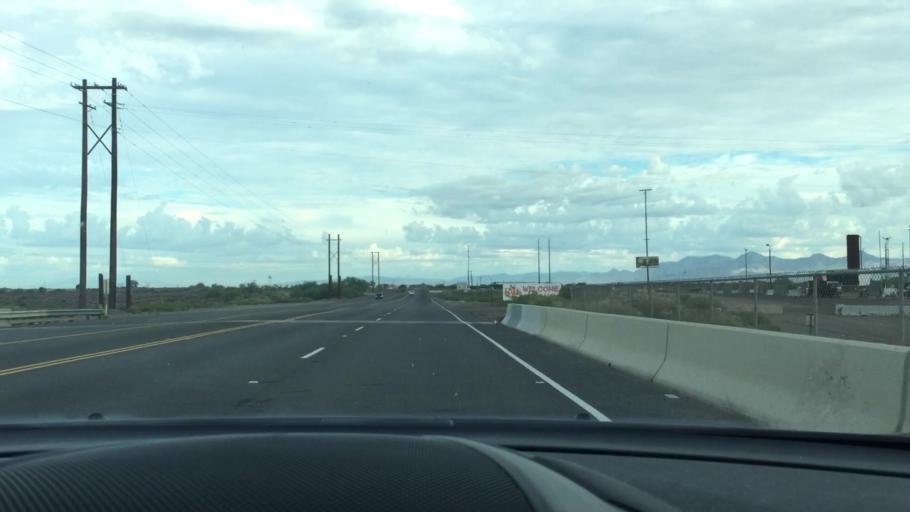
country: US
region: Arizona
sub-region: Maricopa County
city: Mesa
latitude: 33.4485
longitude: -111.8567
